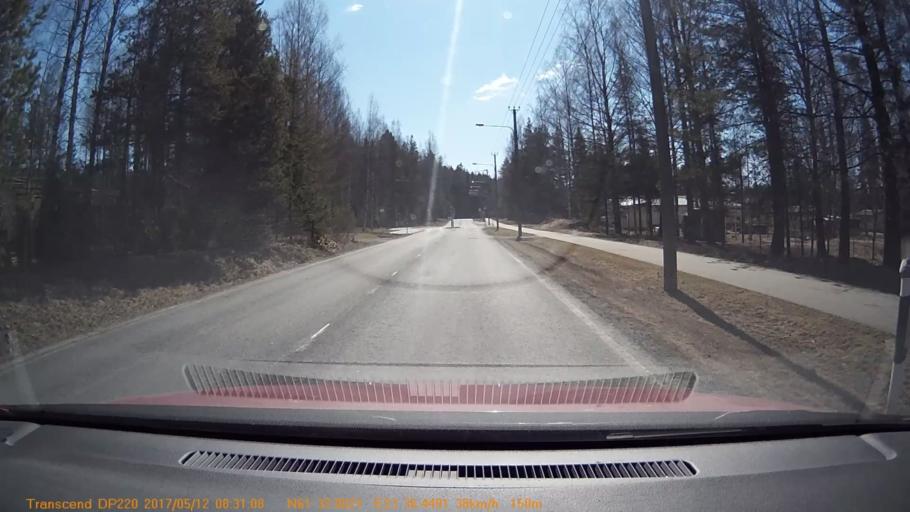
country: FI
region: Pirkanmaa
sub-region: Tampere
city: Yloejaervi
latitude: 61.5335
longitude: 23.6073
